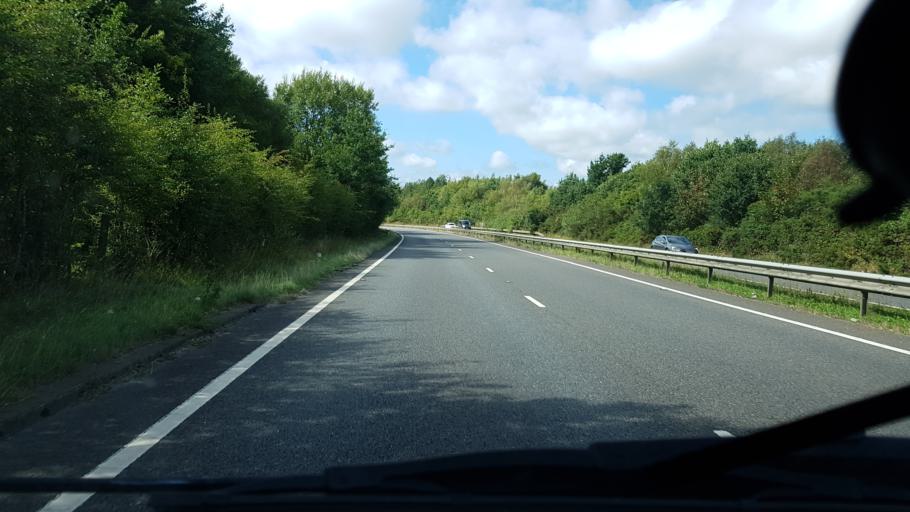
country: GB
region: England
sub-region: West Sussex
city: Broadfield
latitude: 51.0933
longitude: -0.2140
